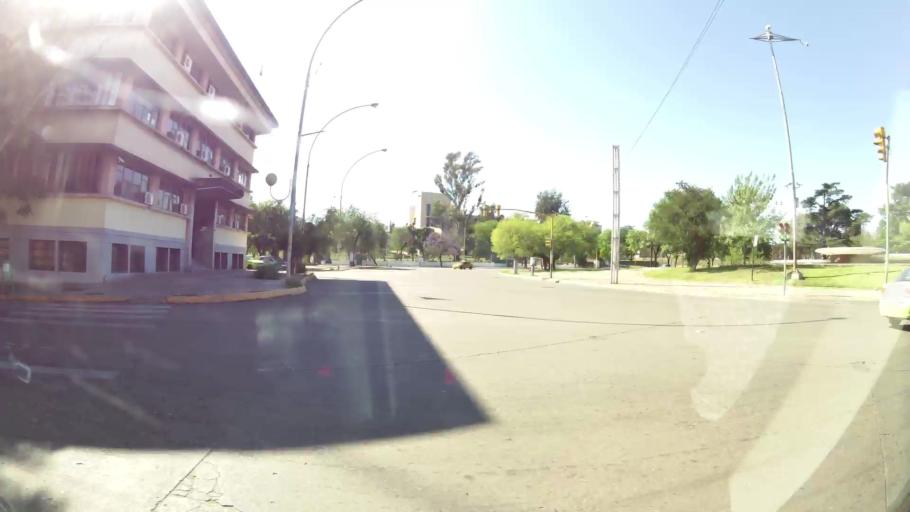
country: AR
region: Cordoba
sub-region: Departamento de Capital
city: Cordoba
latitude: -31.4324
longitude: -64.1941
